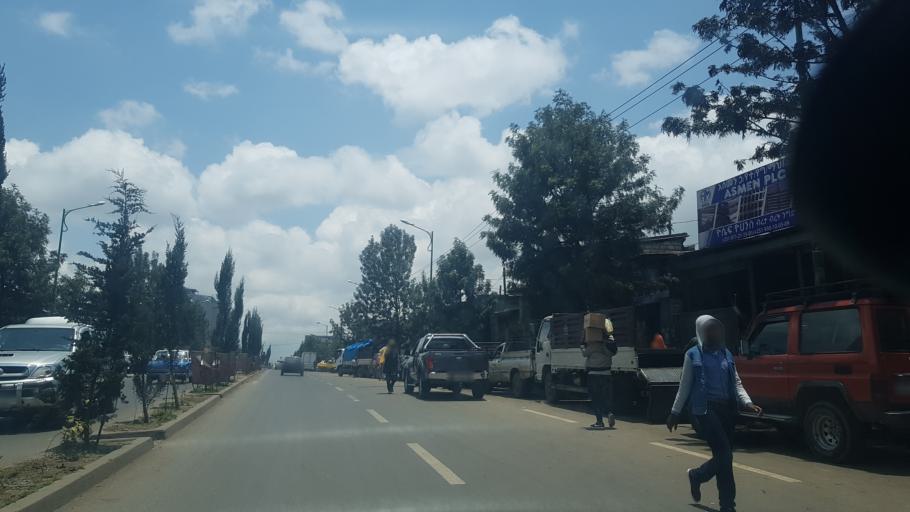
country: ET
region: Adis Abeba
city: Addis Ababa
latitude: 9.0238
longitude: 38.7366
